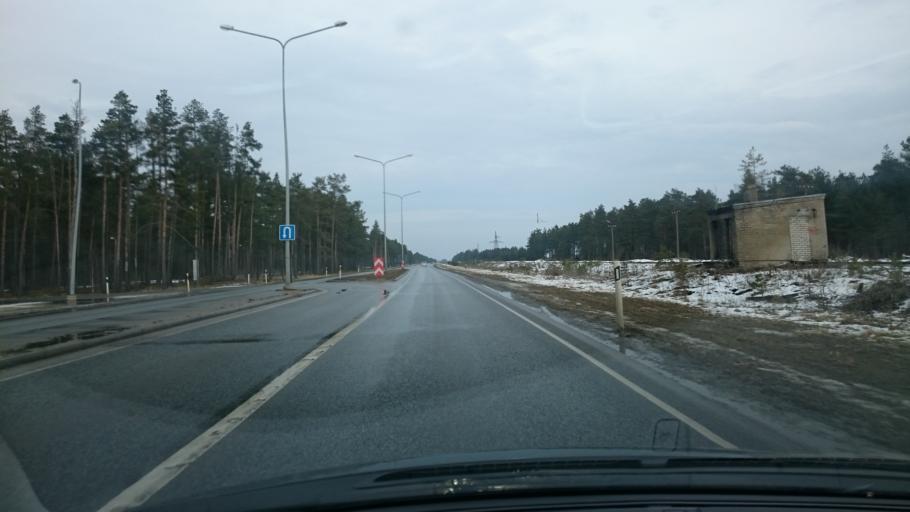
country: EE
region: Harju
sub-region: Saku vald
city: Saku
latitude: 59.3430
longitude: 24.7039
